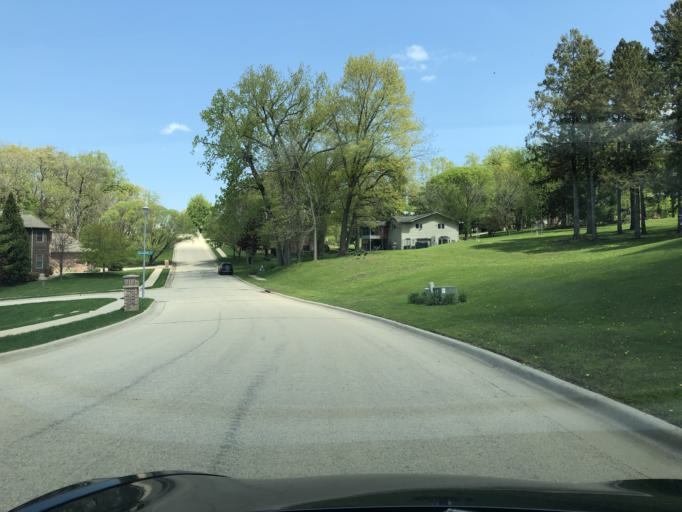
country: US
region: Iowa
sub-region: Dubuque County
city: Dubuque
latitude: 42.4764
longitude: -90.6629
